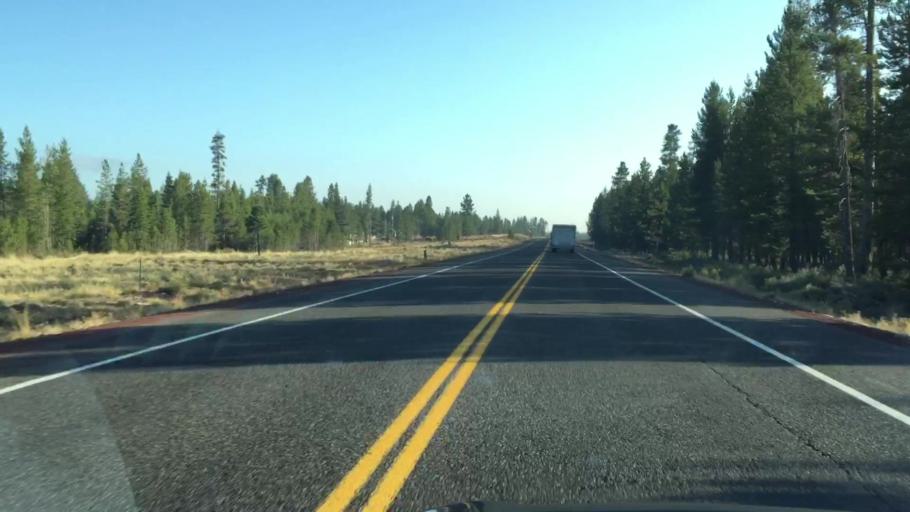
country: US
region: Oregon
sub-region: Deschutes County
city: La Pine
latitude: 43.4411
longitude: -121.7103
